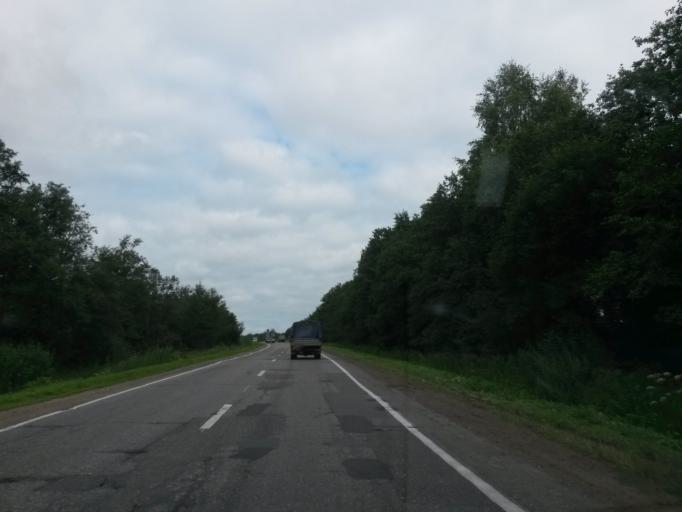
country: RU
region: Jaroslavl
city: Gavrilov-Yam
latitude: 57.4385
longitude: 39.9175
